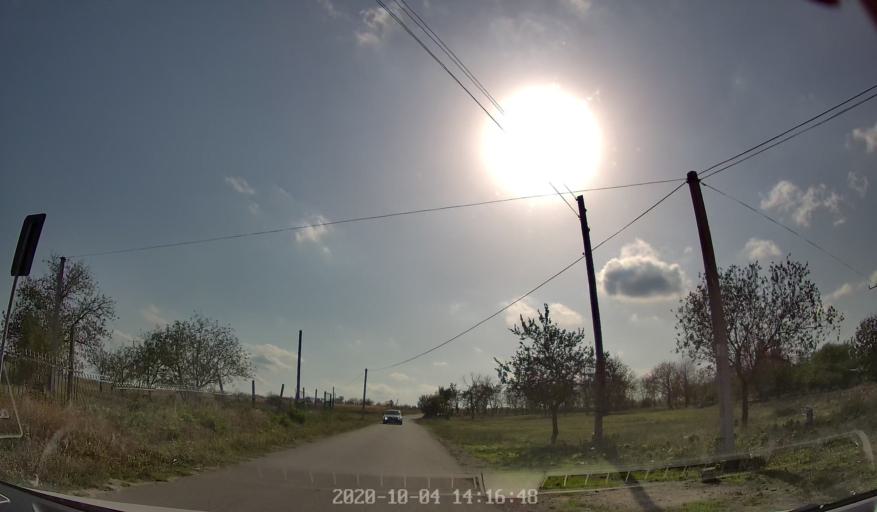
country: MD
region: Rezina
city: Saharna
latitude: 47.6029
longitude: 28.9843
